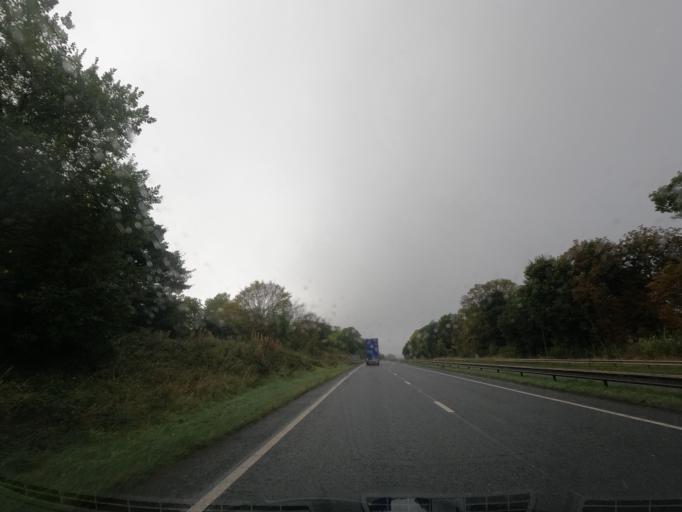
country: GB
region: England
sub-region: Redcar and Cleveland
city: South Bank
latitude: 54.5461
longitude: -1.1585
